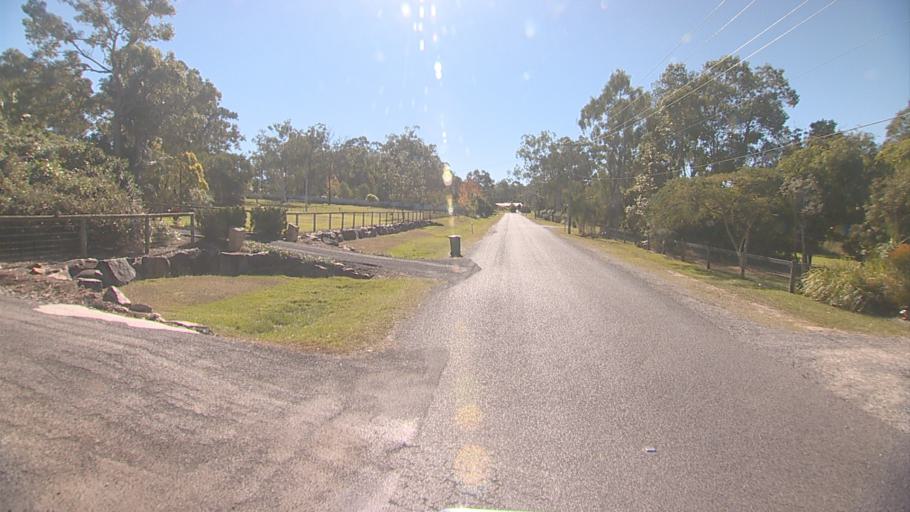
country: AU
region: Queensland
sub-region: Logan
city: Park Ridge South
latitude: -27.7116
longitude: 153.0413
